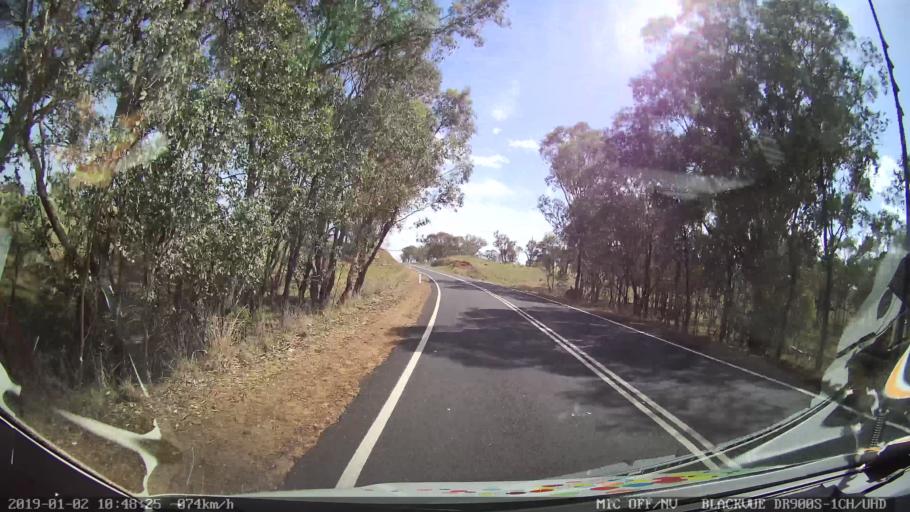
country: AU
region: New South Wales
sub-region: Cootamundra
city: Cootamundra
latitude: -34.7370
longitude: 148.2780
